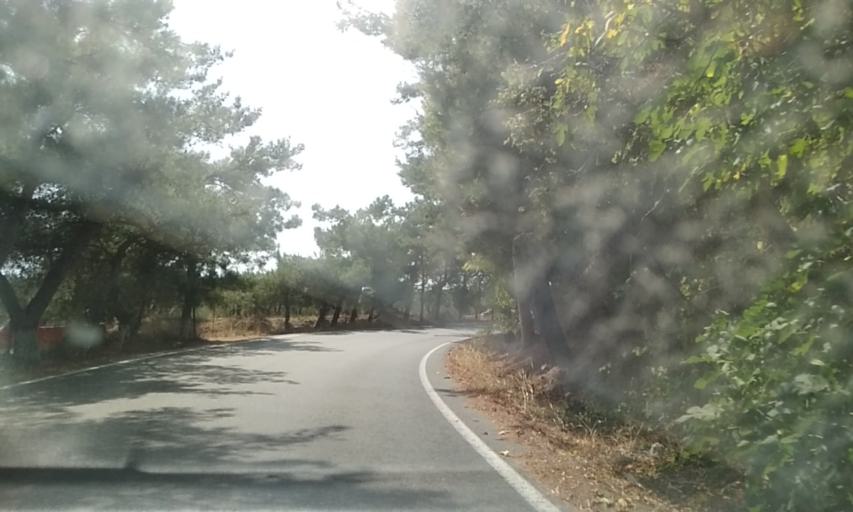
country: GR
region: Crete
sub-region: Nomos Lasithiou
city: Siteia
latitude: 35.1299
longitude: 26.0739
